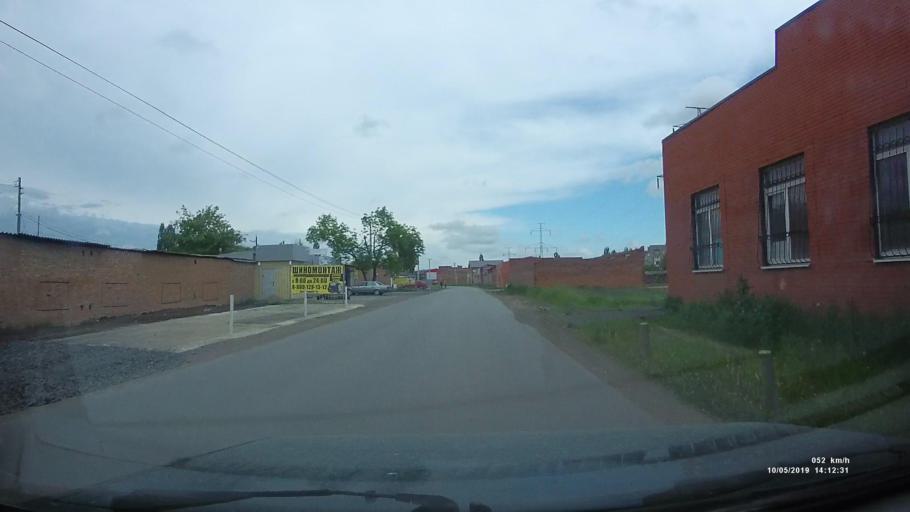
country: RU
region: Rostov
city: Azov
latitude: 47.0925
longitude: 39.4266
